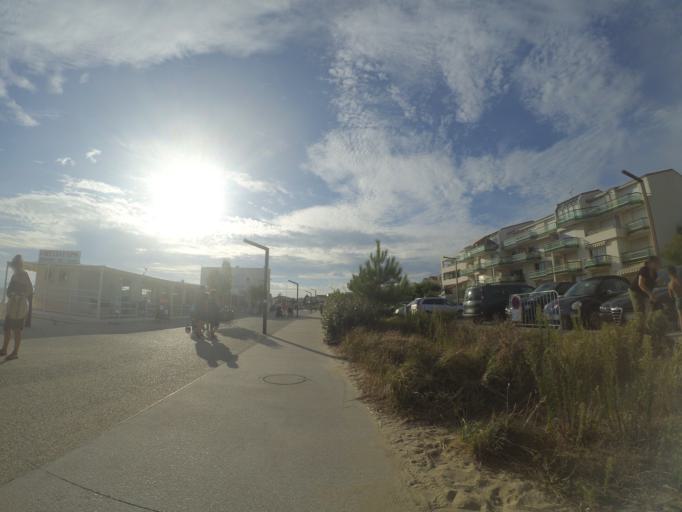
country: FR
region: Poitou-Charentes
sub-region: Departement de la Charente-Maritime
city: Saint-Georges-de-Didonne
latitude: 45.6005
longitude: -0.9967
